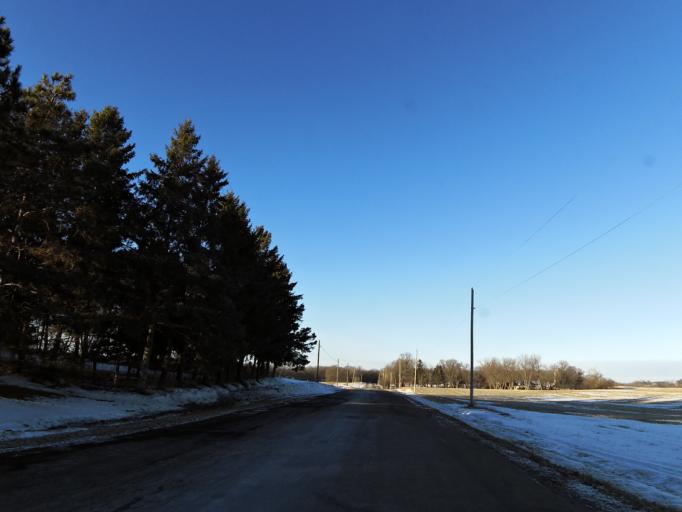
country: US
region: Minnesota
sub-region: Washington County
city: Cottage Grove
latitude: 44.8264
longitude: -92.8831
